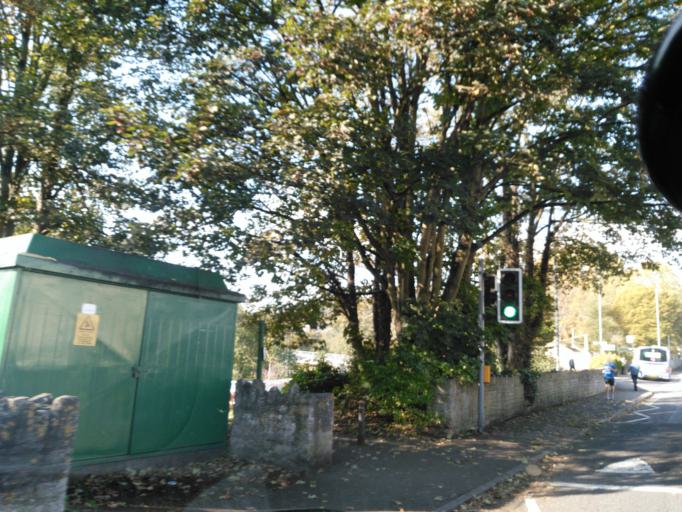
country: GB
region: England
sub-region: Bath and North East Somerset
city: Bath
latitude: 51.4052
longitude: -2.3170
